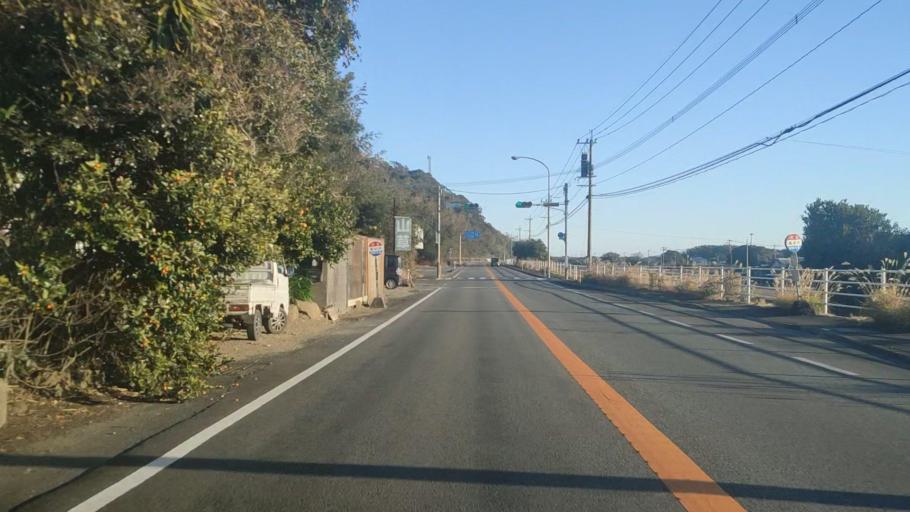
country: JP
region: Miyazaki
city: Takanabe
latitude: 32.1029
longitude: 131.5216
